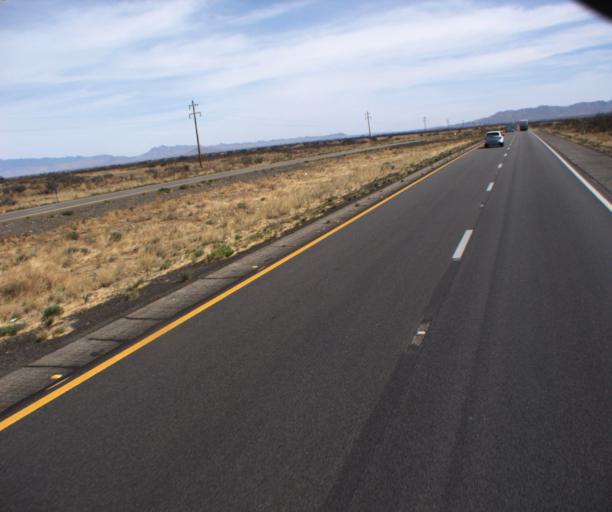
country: US
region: Arizona
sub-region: Cochise County
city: Willcox
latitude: 32.1875
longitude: -109.9305
